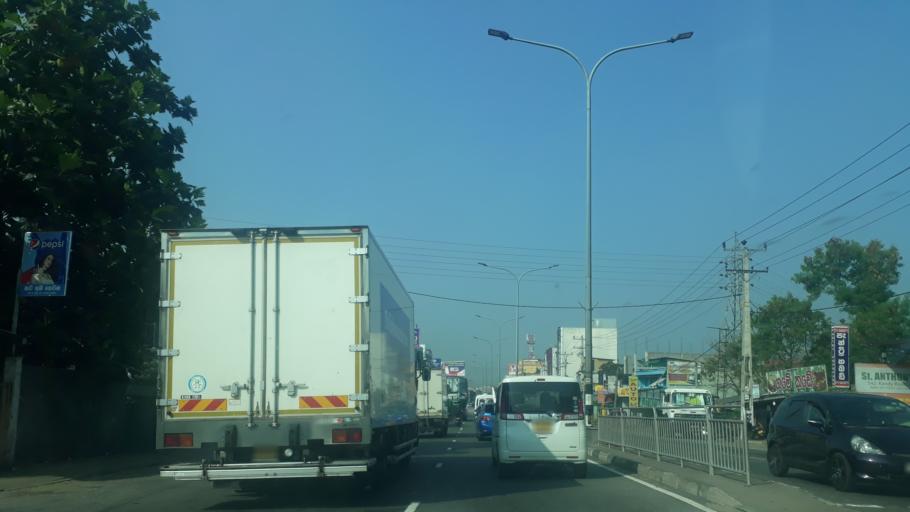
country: LK
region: Western
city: Kelaniya
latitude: 6.9684
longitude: 79.9105
